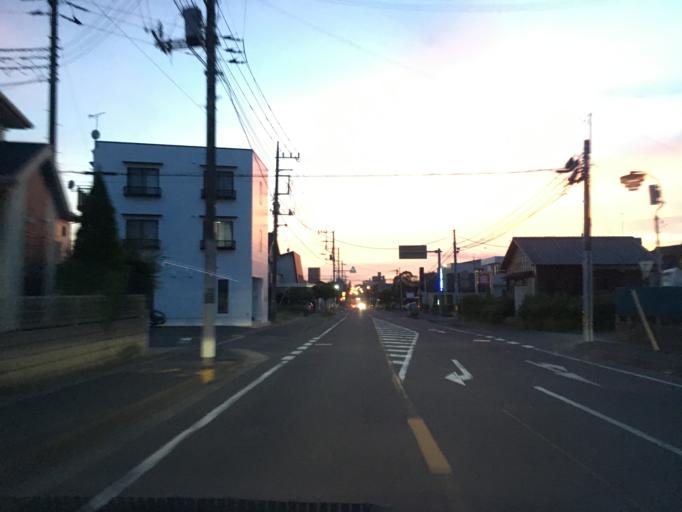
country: JP
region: Ibaraki
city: Katsuta
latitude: 36.3879
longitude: 140.5444
